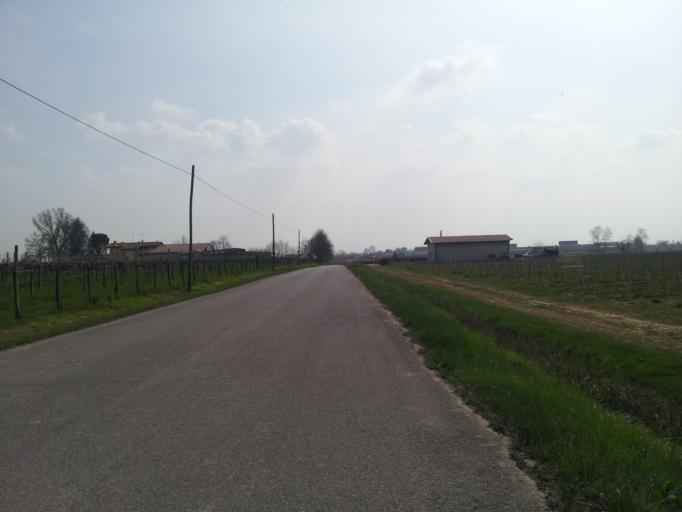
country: IT
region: Friuli Venezia Giulia
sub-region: Provincia di Pordenone
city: Cecchini
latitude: 45.8803
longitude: 12.6419
